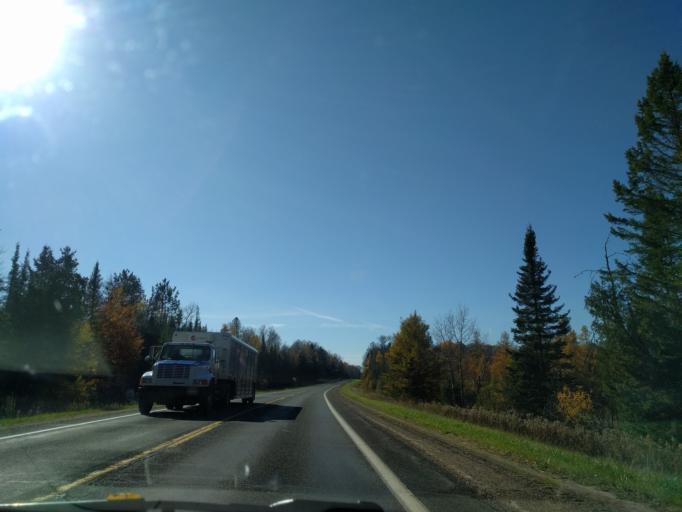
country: US
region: Michigan
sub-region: Iron County
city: Crystal Falls
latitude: 46.1745
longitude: -88.0543
